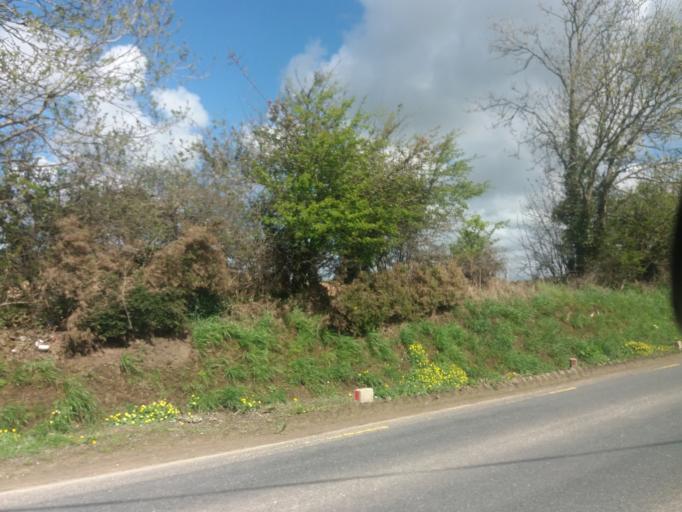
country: IE
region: Leinster
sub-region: Loch Garman
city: Loch Garman
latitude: 52.2864
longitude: -6.6235
